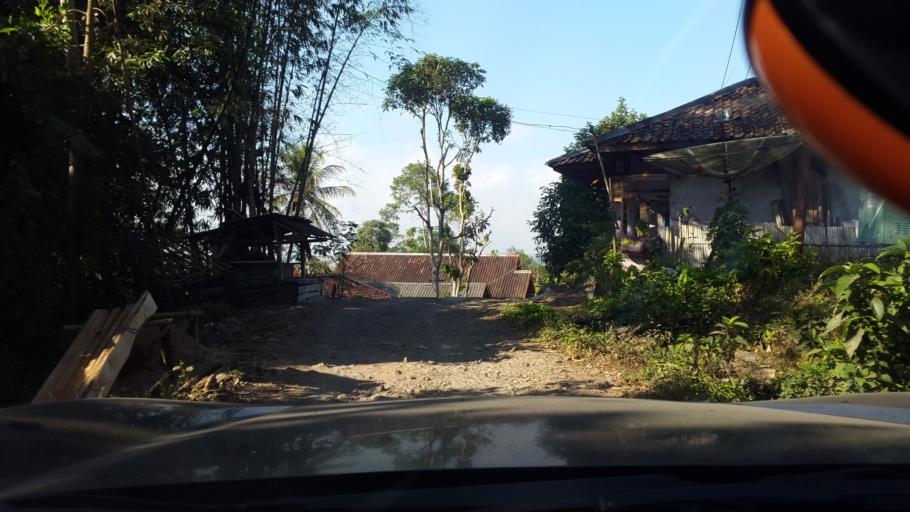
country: ID
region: West Java
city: Curugkembar Satu
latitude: -7.2173
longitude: 106.9392
